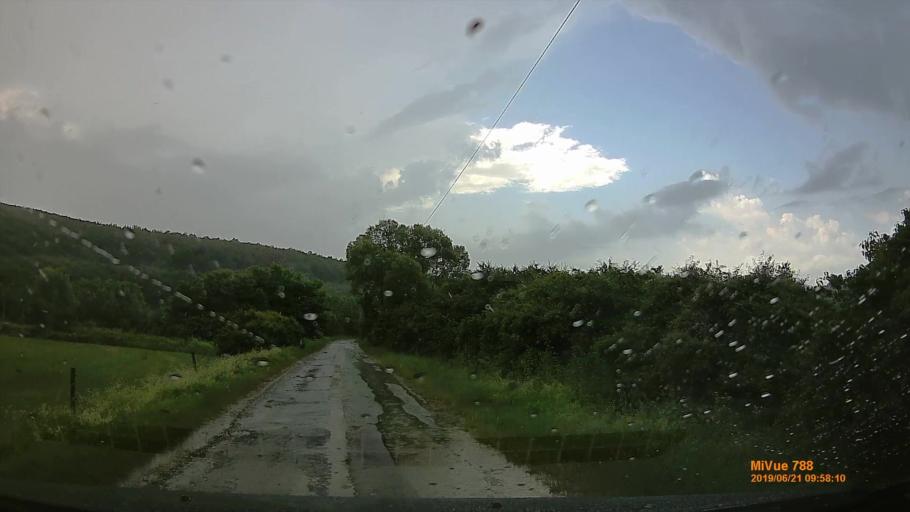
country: HU
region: Baranya
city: Buekkoesd
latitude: 46.2172
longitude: 17.9712
